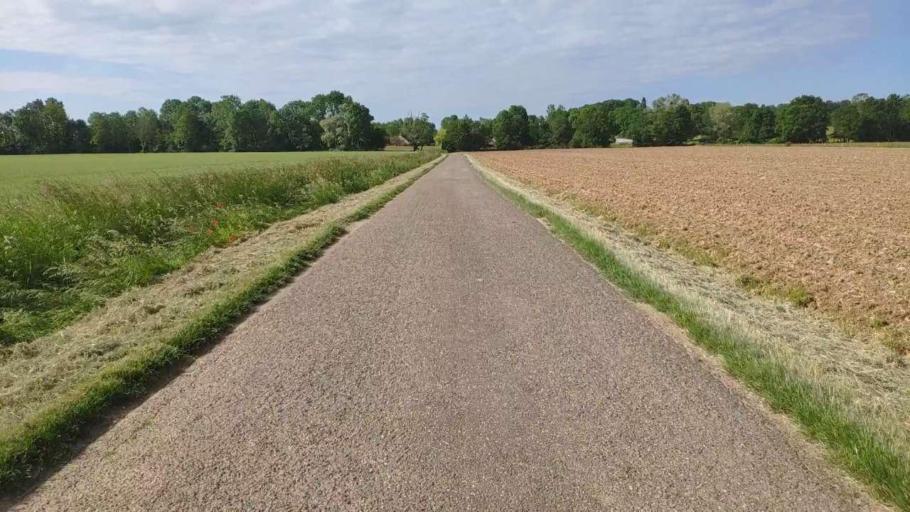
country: FR
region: Franche-Comte
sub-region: Departement du Jura
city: Bletterans
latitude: 46.7207
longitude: 5.4618
